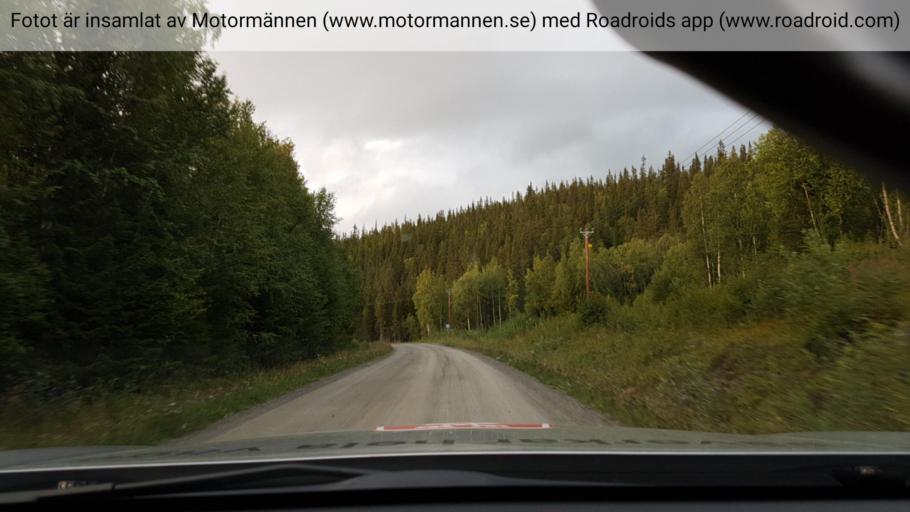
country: SE
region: Vaesterbotten
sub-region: Vilhelmina Kommun
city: Sjoberg
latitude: 65.5788
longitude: 15.2999
